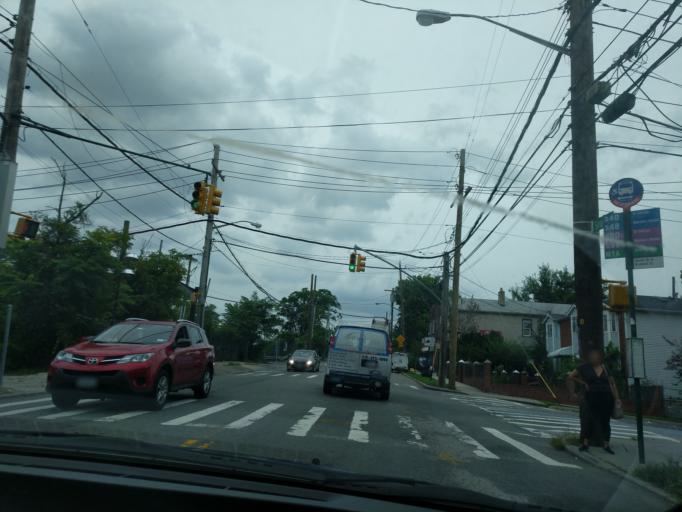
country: US
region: New York
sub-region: Richmond County
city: Bloomfield
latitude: 40.6320
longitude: -74.1663
